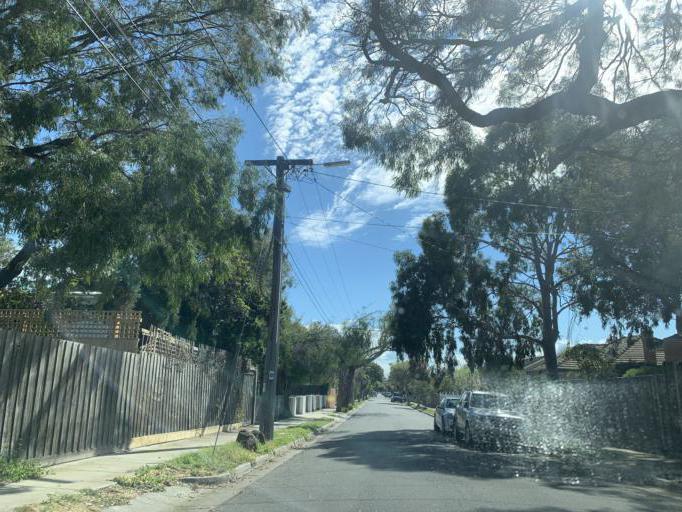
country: AU
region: Victoria
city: Hampton
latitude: -37.9488
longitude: 145.0152
